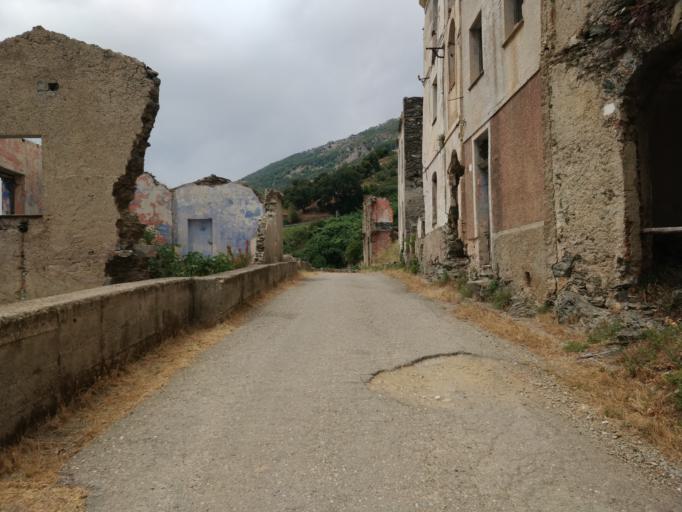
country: IT
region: Sardinia
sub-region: Provincia di Ogliastra
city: Gairo Sant'Elena
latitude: 39.8473
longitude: 9.4999
